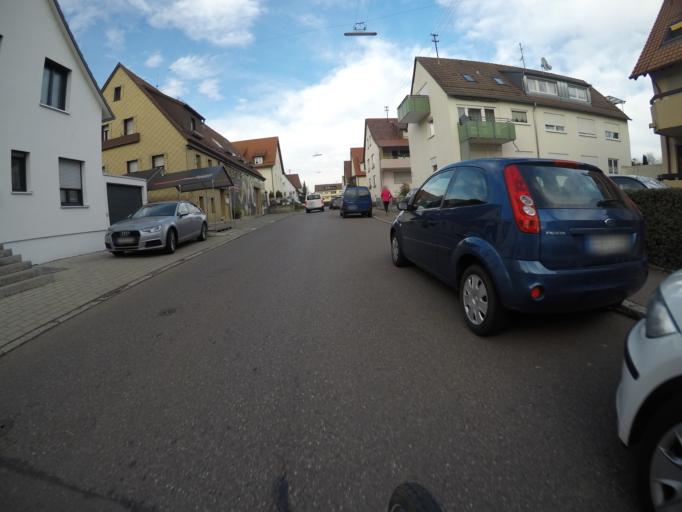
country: DE
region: Baden-Wuerttemberg
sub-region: Regierungsbezirk Stuttgart
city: Leinfelden-Echterdingen
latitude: 48.6903
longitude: 9.1645
